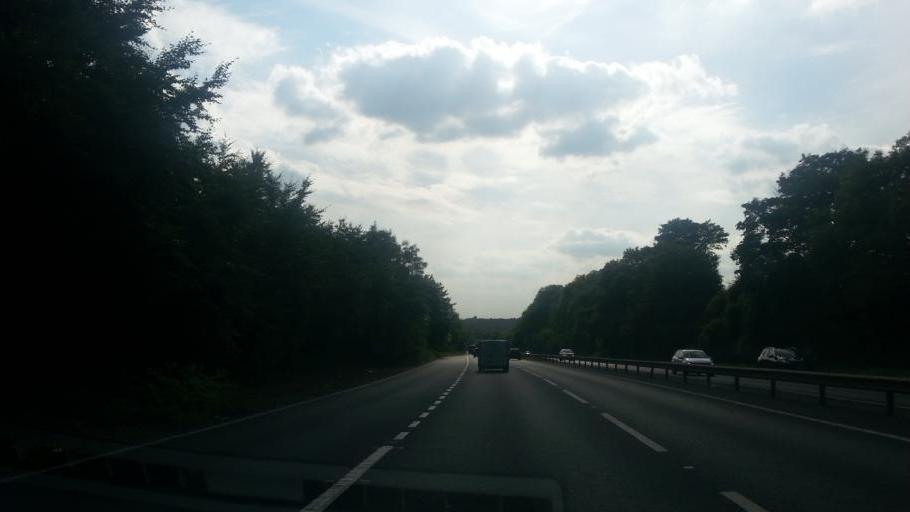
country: GB
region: England
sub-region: Surrey
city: Godalming
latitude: 51.2271
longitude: -0.6226
